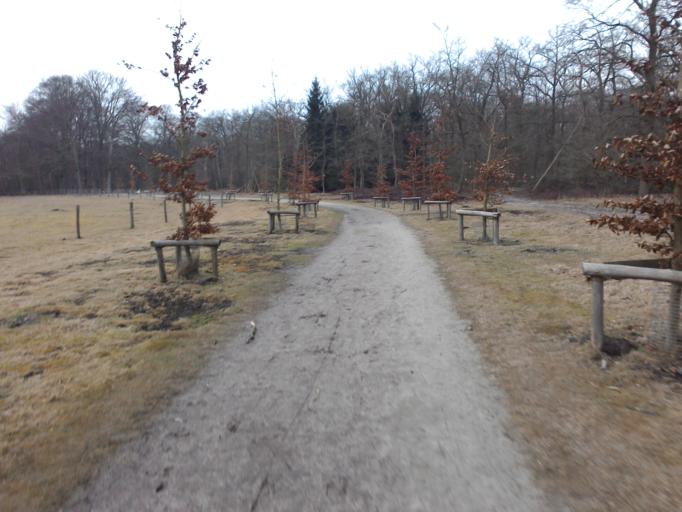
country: NL
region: Utrecht
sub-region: Gemeente De Bilt
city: De Bilt
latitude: 52.1073
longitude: 5.2006
